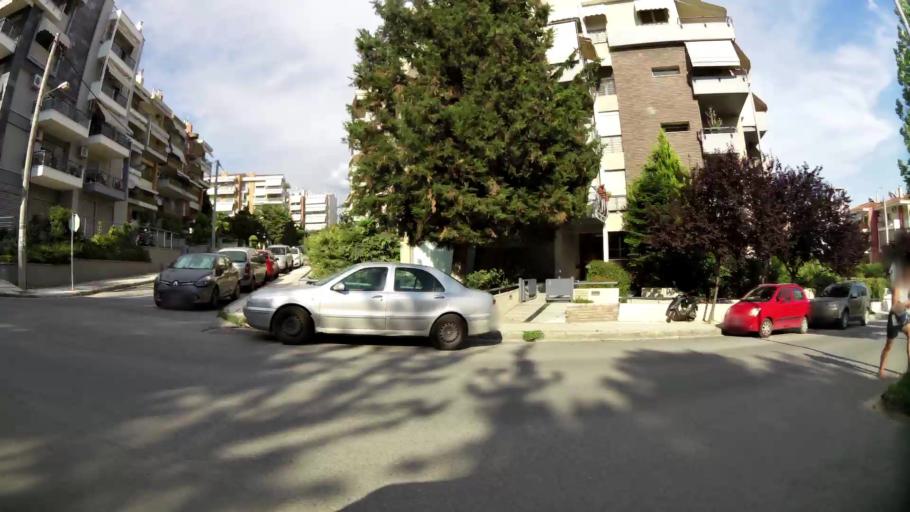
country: GR
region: Central Macedonia
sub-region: Nomos Thessalonikis
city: Kalamaria
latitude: 40.5713
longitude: 22.9665
